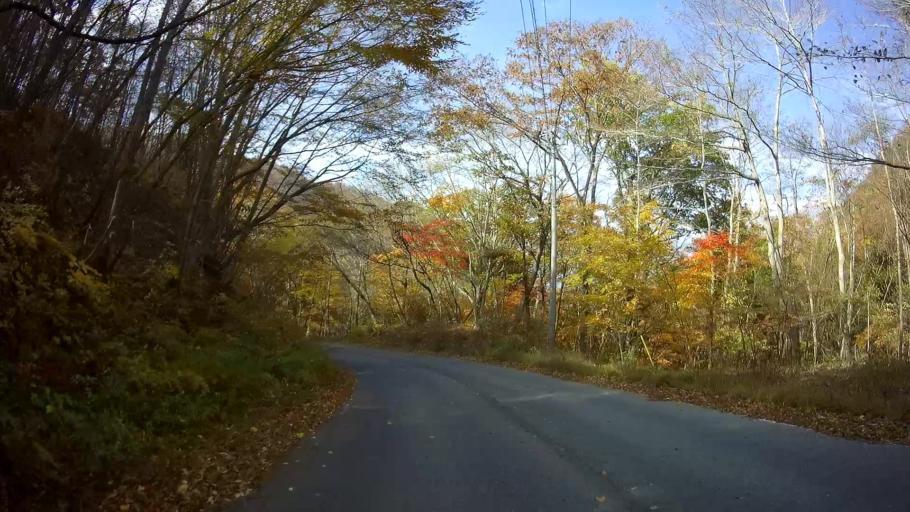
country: JP
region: Gunma
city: Nakanojomachi
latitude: 36.5208
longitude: 138.6618
